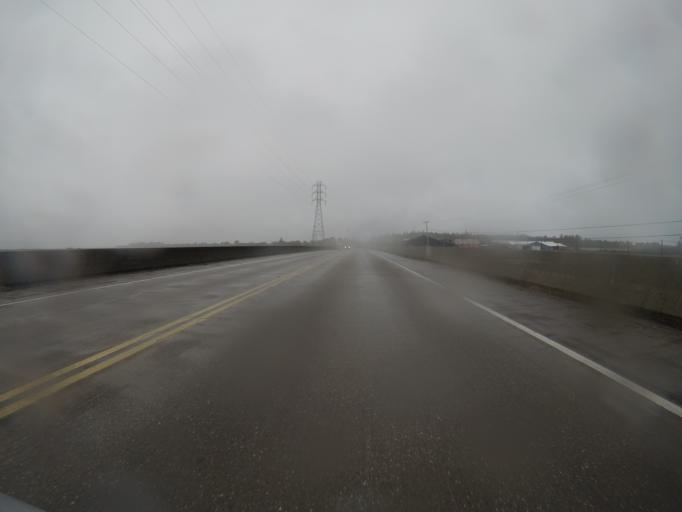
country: US
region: California
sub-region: Humboldt County
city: Eureka
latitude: 40.8653
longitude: -124.1493
